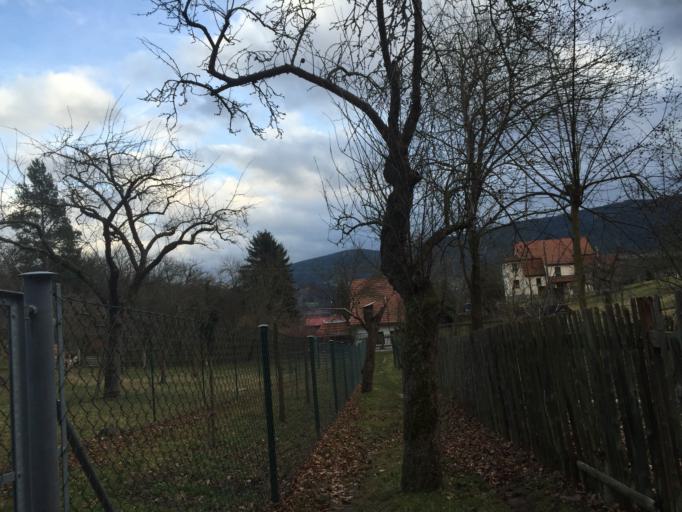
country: DE
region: Thuringia
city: Bad Blankenburg
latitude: 50.6883
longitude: 11.2673
